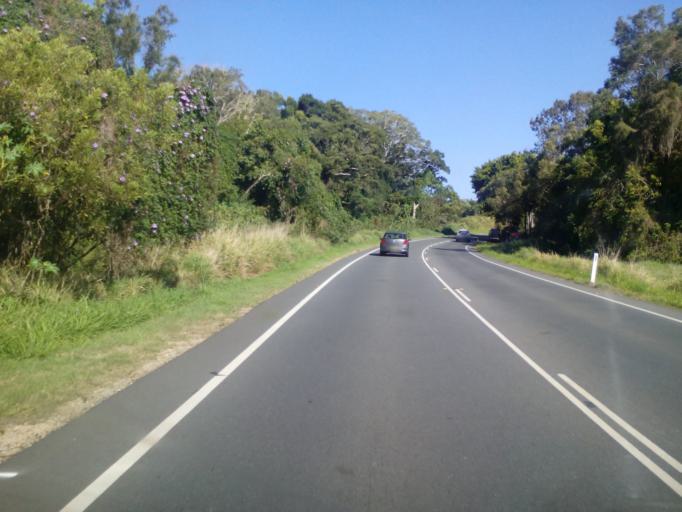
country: AU
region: New South Wales
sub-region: Tweed
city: Kingscliff
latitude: -28.2608
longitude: 153.5615
